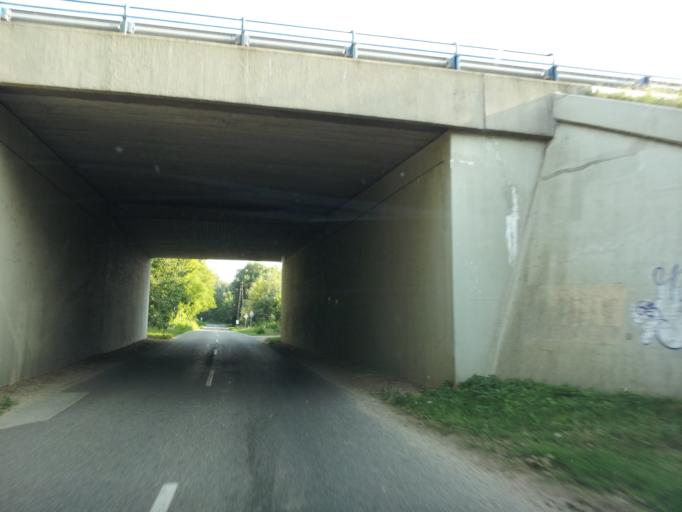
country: HU
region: Somogy
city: Zamardi
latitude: 46.8826
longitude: 18.0030
